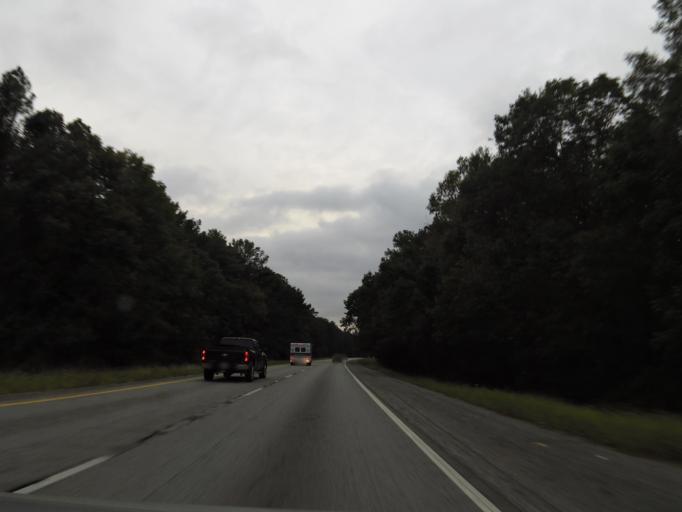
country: US
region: Alabama
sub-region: Saint Clair County
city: Springville
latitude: 33.7900
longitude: -86.3882
